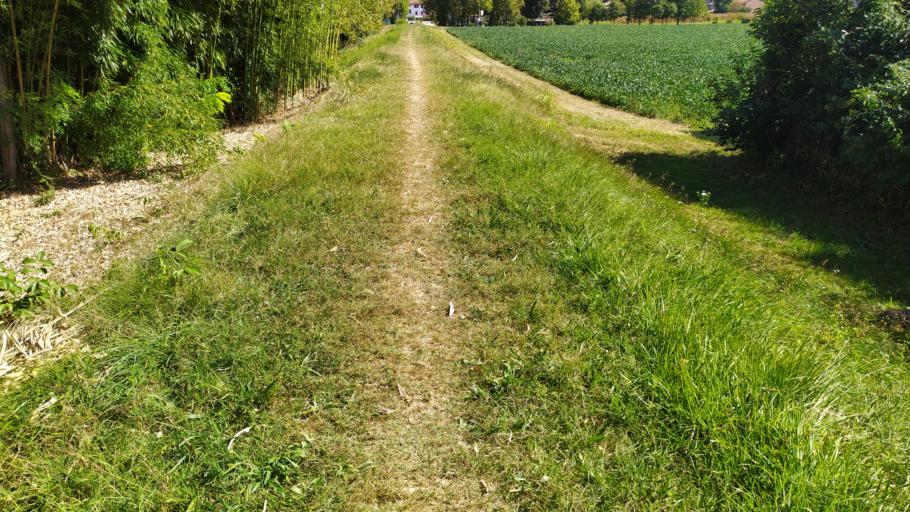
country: IT
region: Friuli Venezia Giulia
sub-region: Provincia di Pordenone
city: Cavolano-Schiavoi
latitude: 45.9393
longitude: 12.4938
